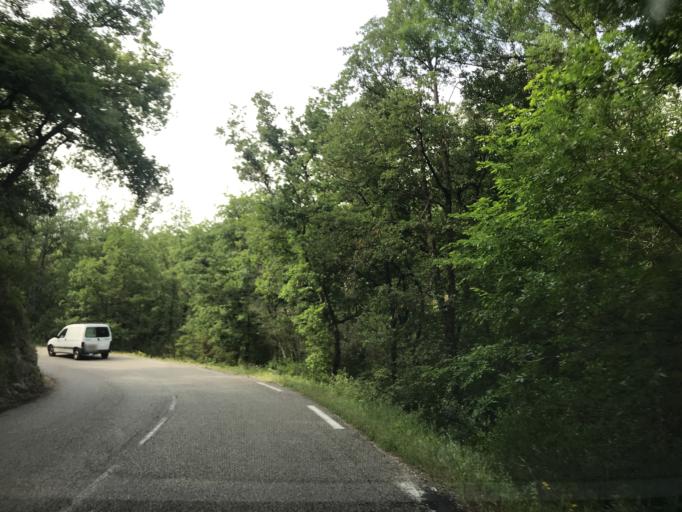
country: FR
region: Provence-Alpes-Cote d'Azur
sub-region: Departement du Var
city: Rians
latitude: 43.6410
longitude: 5.7608
